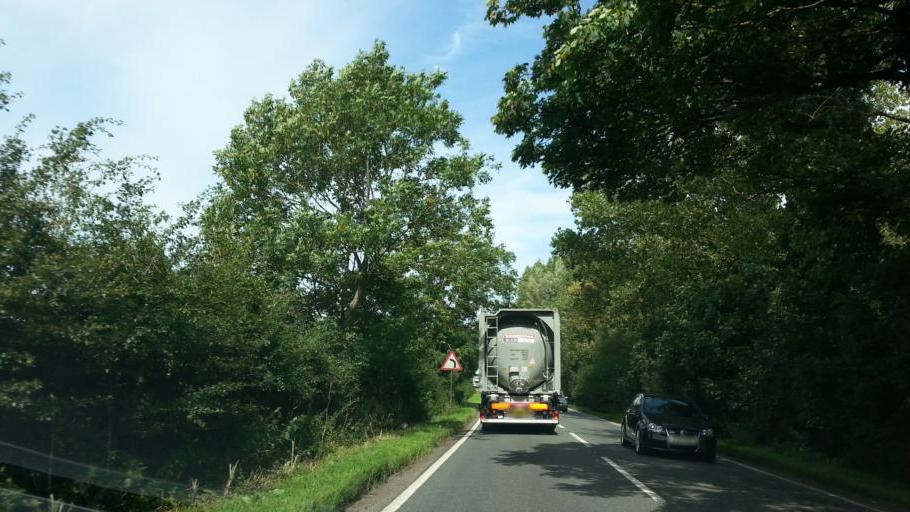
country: GB
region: England
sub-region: Suffolk
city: Exning
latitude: 52.2746
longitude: 0.3937
